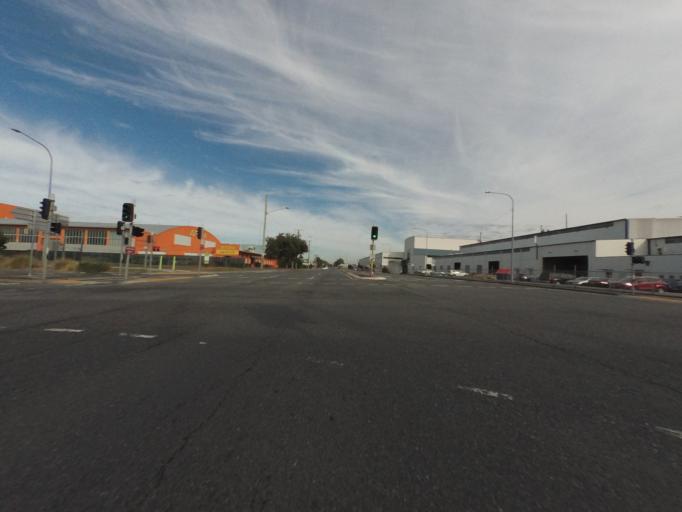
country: AU
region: Queensland
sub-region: Brisbane
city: Ascot
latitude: -27.4302
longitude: 153.0931
